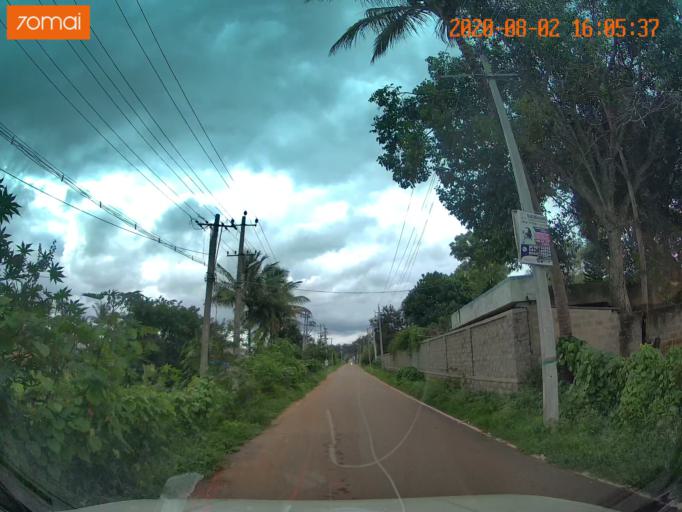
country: IN
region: Karnataka
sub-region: Bangalore Urban
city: Anekal
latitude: 12.8341
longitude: 77.6393
